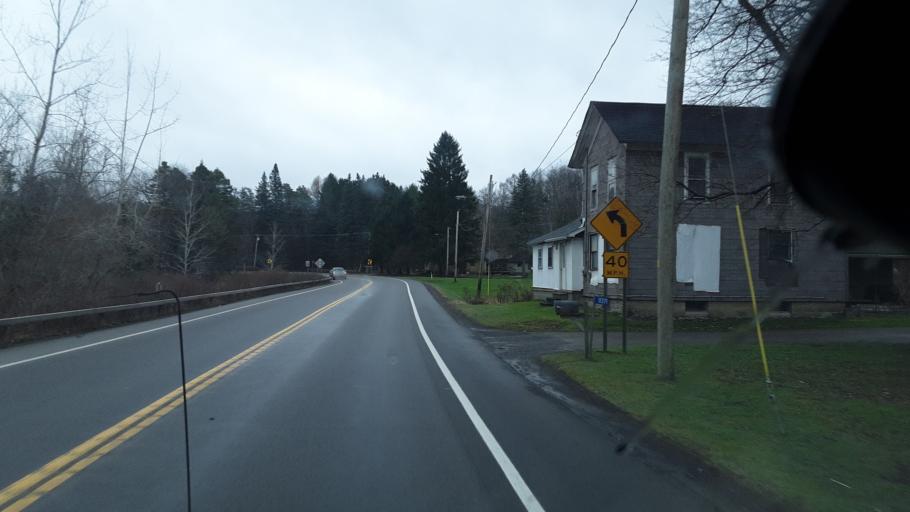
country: US
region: New York
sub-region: Wyoming County
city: Arcade
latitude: 42.4912
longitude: -78.3806
